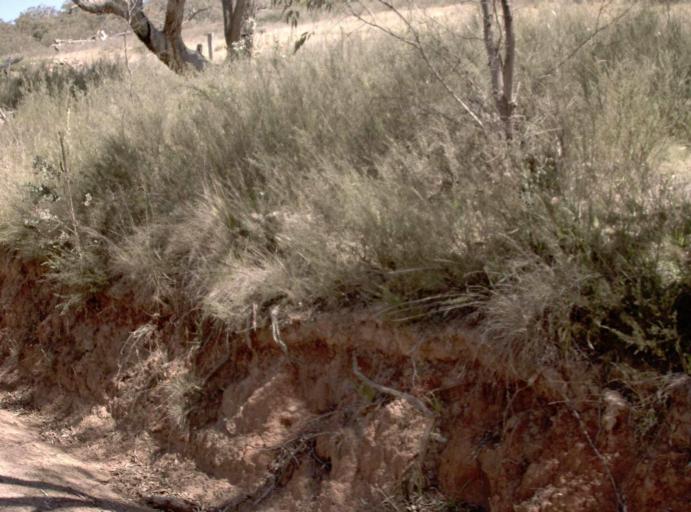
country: AU
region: New South Wales
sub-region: Snowy River
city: Jindabyne
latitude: -37.0608
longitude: 148.5737
